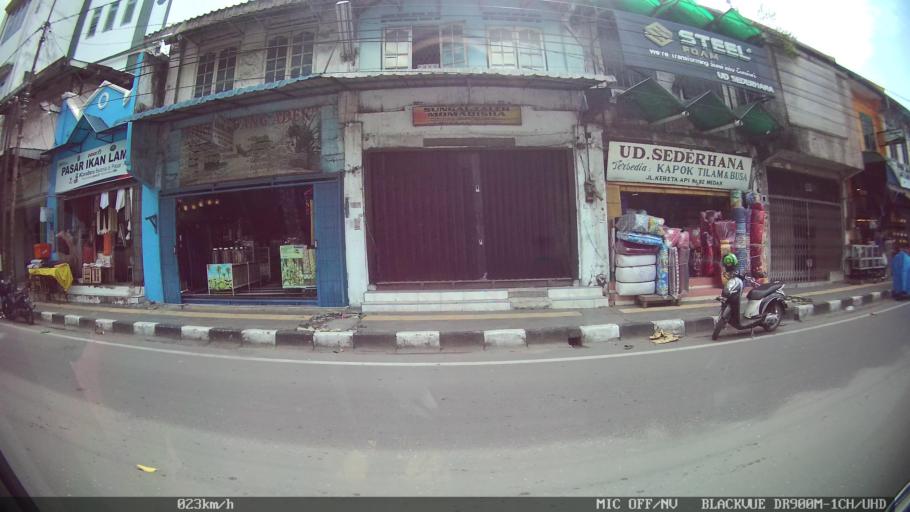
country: ID
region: North Sumatra
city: Medan
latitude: 3.5874
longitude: 98.6811
